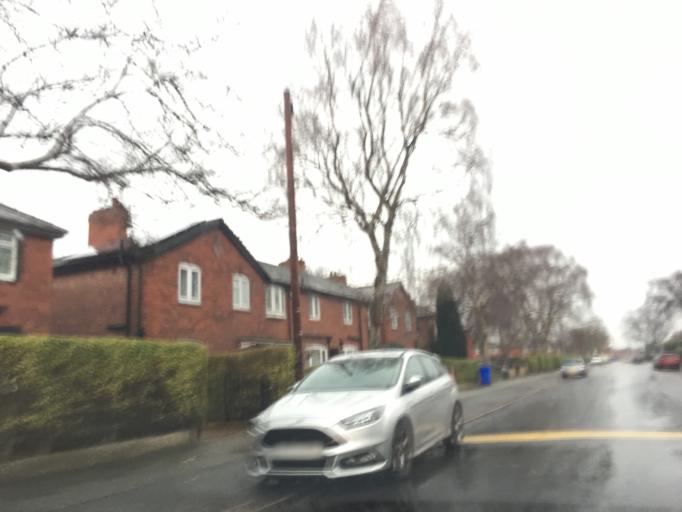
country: GB
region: England
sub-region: Manchester
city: Chorlton cum Hardy
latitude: 53.4260
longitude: -2.2648
